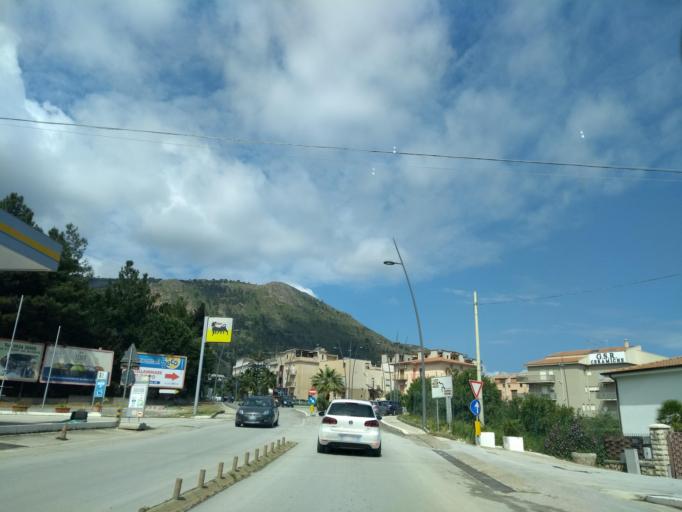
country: IT
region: Sicily
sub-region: Trapani
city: Castellammare del Golfo
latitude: 38.0168
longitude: 12.8894
